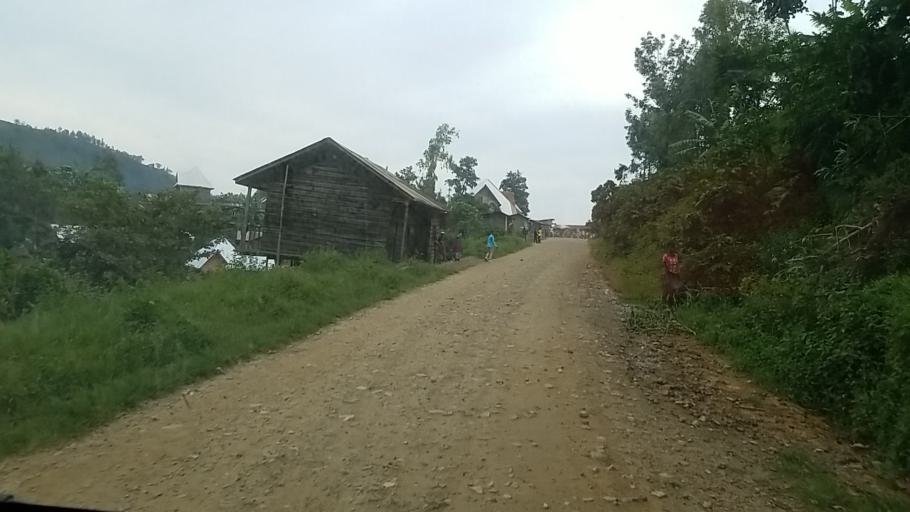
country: CD
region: Nord Kivu
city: Sake
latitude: -1.9577
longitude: 28.9218
